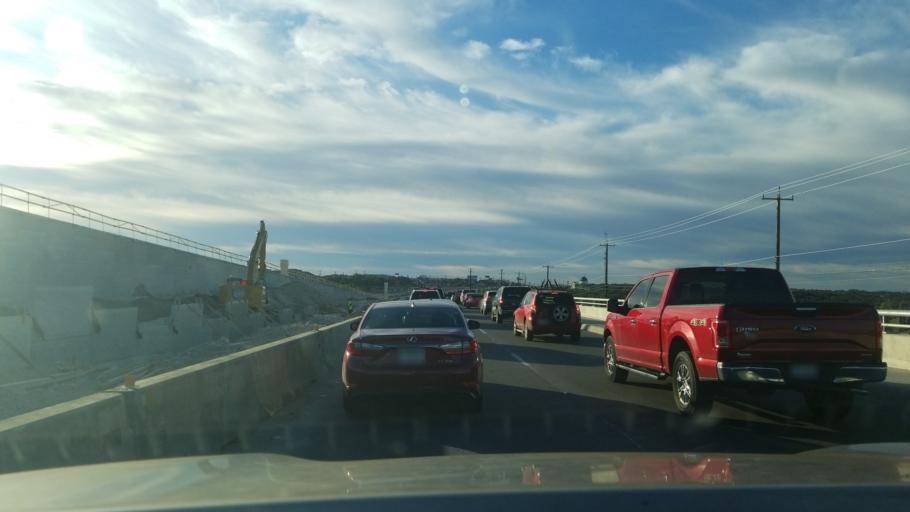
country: US
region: Texas
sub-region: Bexar County
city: Timberwood Park
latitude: 29.6729
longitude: -98.4521
